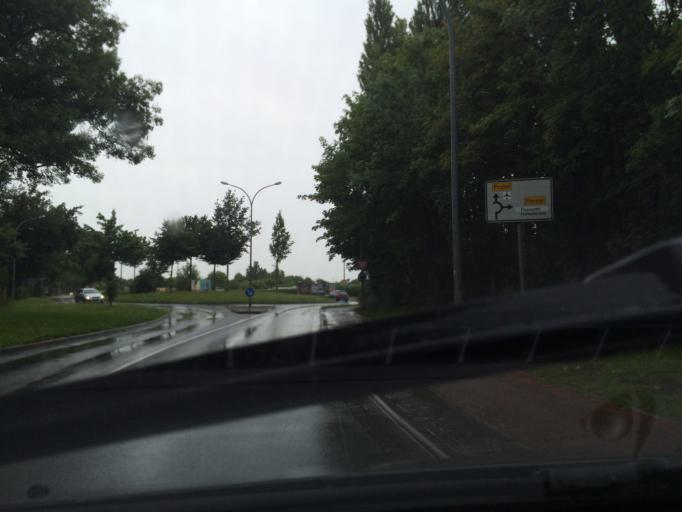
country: DE
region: Mecklenburg-Vorpommern
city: Kramerhof
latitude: 54.3334
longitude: 13.0653
